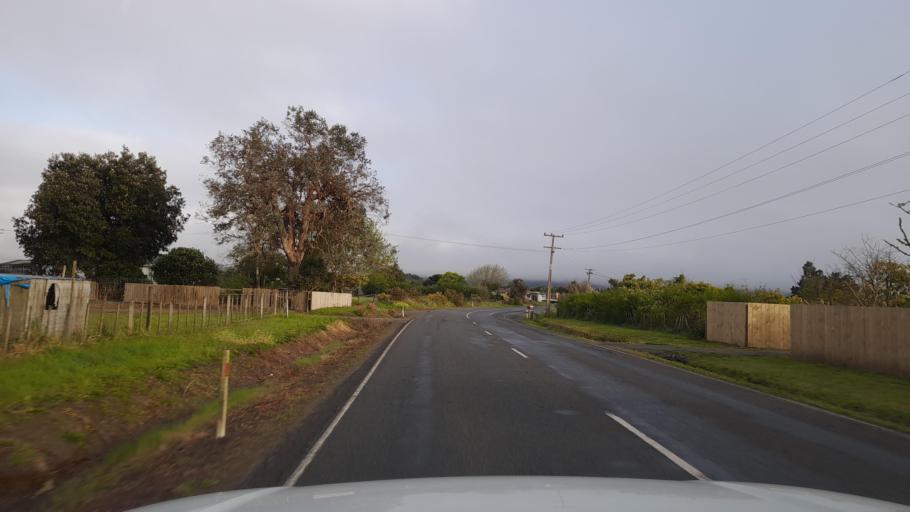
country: NZ
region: Northland
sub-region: Far North District
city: Waimate North
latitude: -35.4228
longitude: 173.8110
